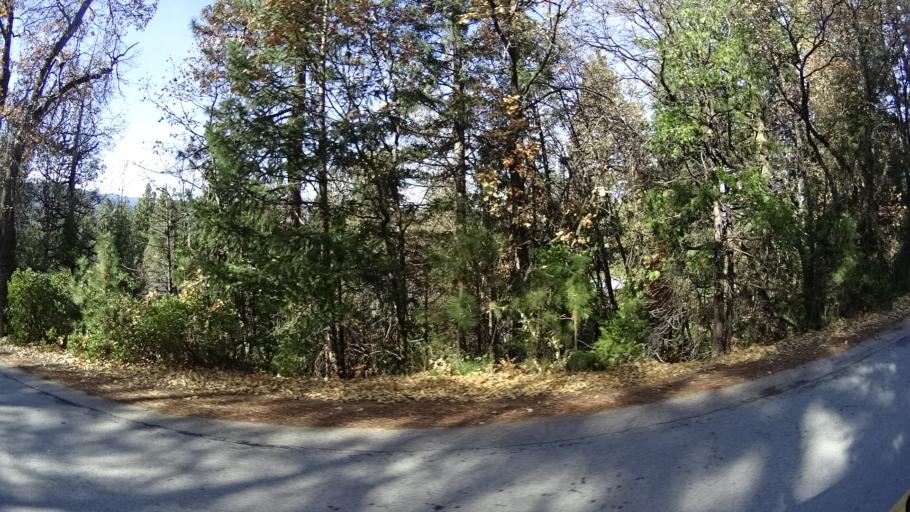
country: US
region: California
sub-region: Siskiyou County
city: Weed
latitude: 41.4315
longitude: -122.4170
